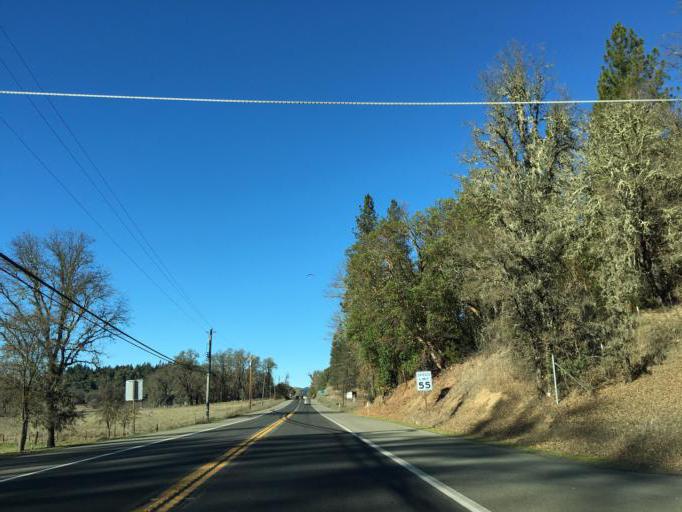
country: US
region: California
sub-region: Mendocino County
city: Laytonville
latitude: 39.6958
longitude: -123.4847
